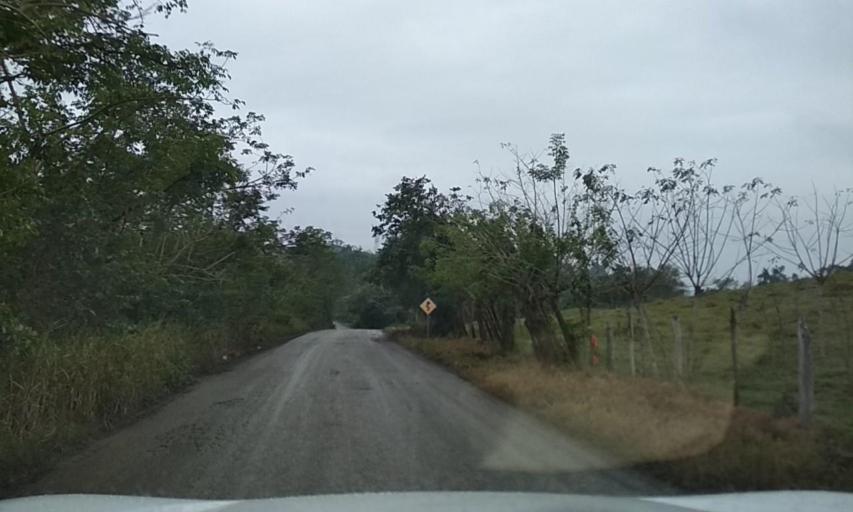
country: MX
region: Veracruz
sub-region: Coatzintla
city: Manuel Maria Contreras
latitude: 20.4621
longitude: -97.4732
